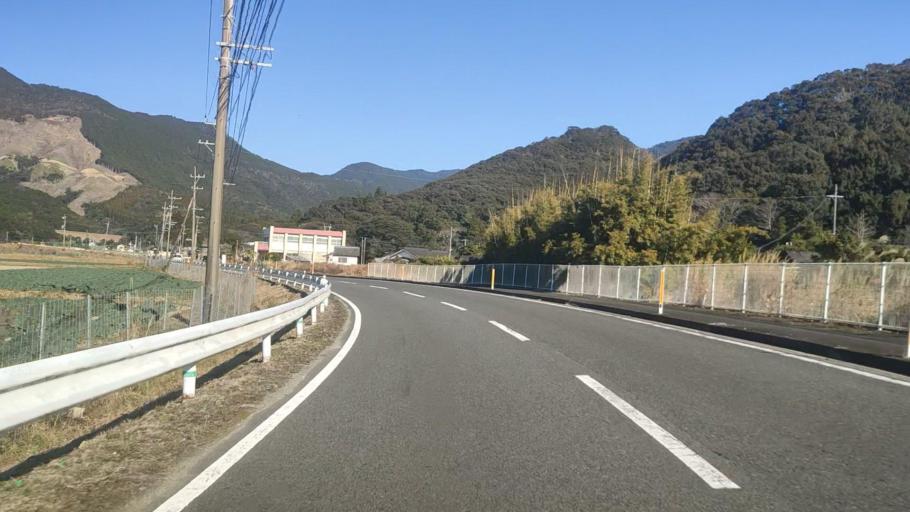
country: JP
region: Miyazaki
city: Nobeoka
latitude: 32.6820
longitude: 131.7875
